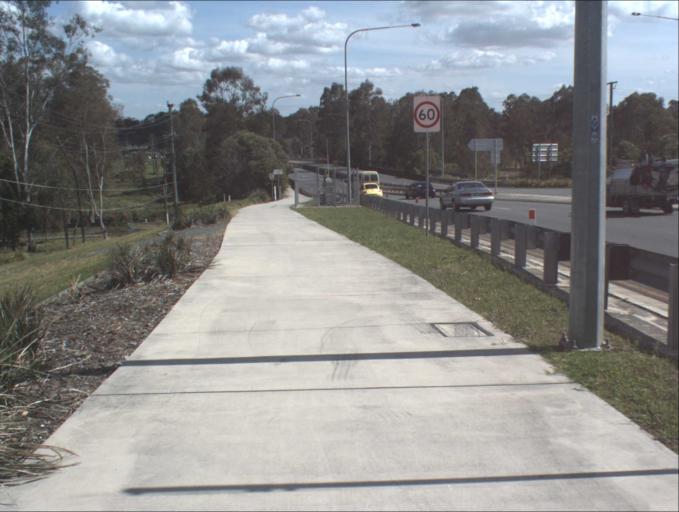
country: AU
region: Queensland
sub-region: Logan
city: Slacks Creek
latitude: -27.6457
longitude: 153.1445
